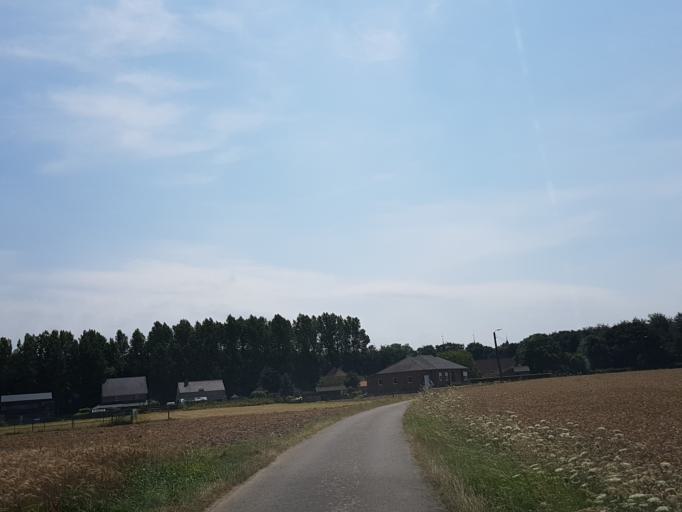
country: BE
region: Flanders
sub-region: Provincie Vlaams-Brabant
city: Steenokkerzeel
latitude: 50.9349
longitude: 4.5032
